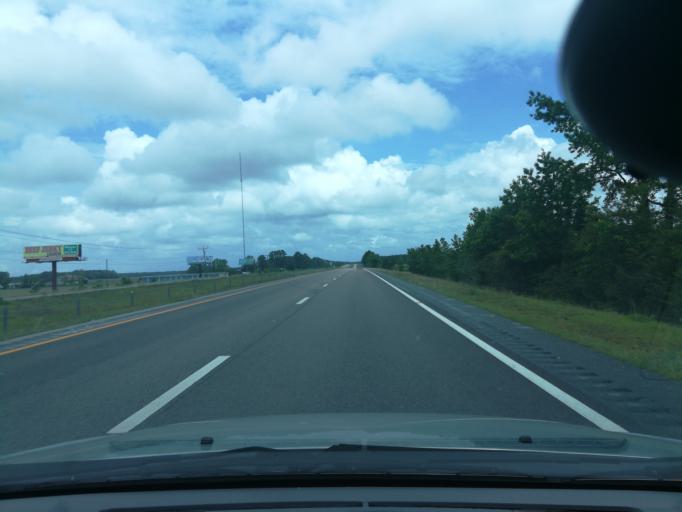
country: US
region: North Carolina
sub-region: Tyrrell County
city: Columbia
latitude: 35.8857
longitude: -76.3637
